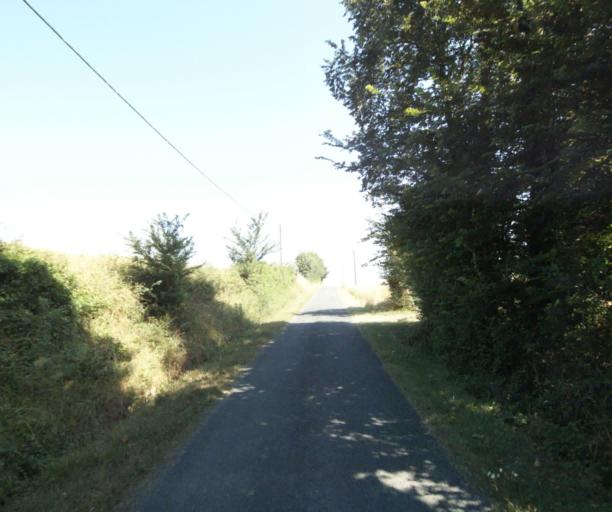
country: FR
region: Midi-Pyrenees
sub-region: Departement de la Haute-Garonne
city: Saint-Felix-Lauragais
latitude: 43.4304
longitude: 1.8508
